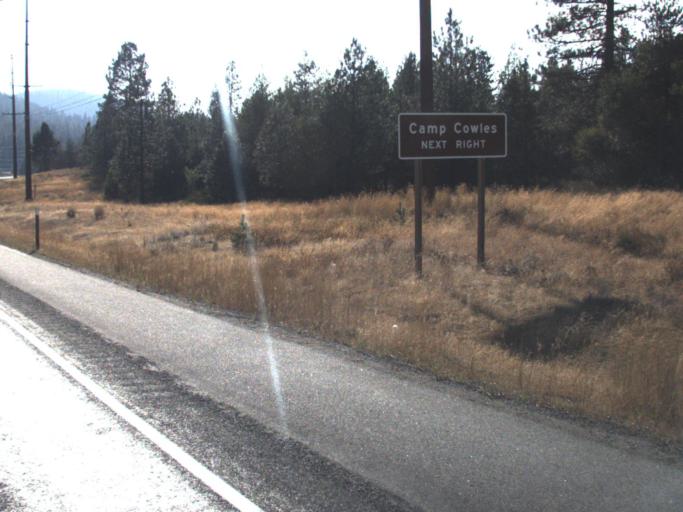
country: US
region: Washington
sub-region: Pend Oreille County
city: Newport
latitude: 48.1013
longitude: -117.2488
